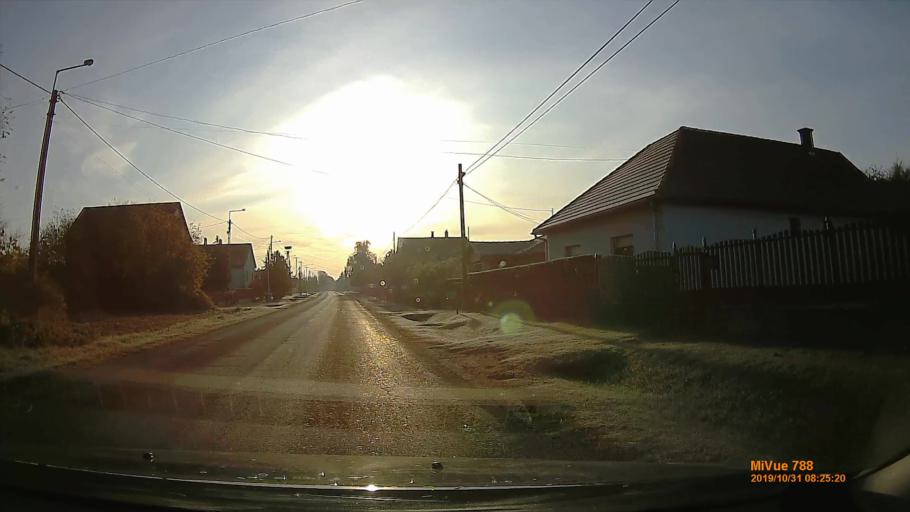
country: HU
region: Pest
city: Tapiobicske
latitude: 47.3665
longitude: 19.6677
